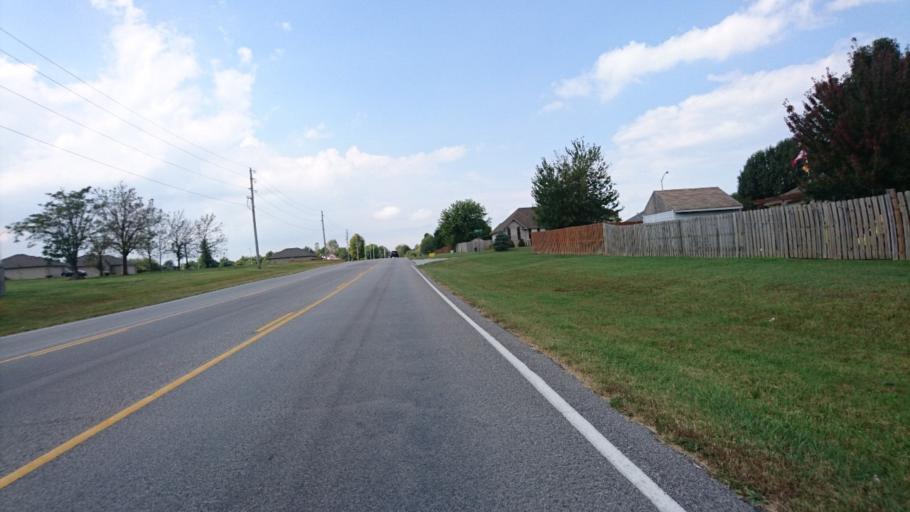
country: US
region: Missouri
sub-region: Greene County
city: Battlefield
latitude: 37.1981
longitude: -93.3943
